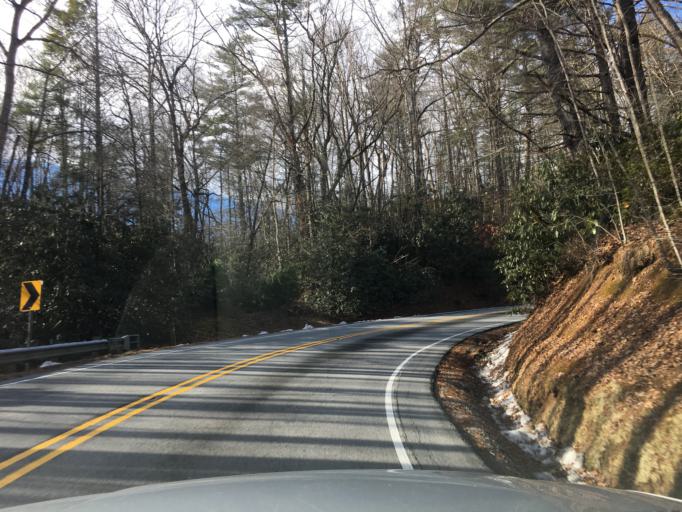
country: US
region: North Carolina
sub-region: Jackson County
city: Cullowhee
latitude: 35.1185
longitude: -83.0062
